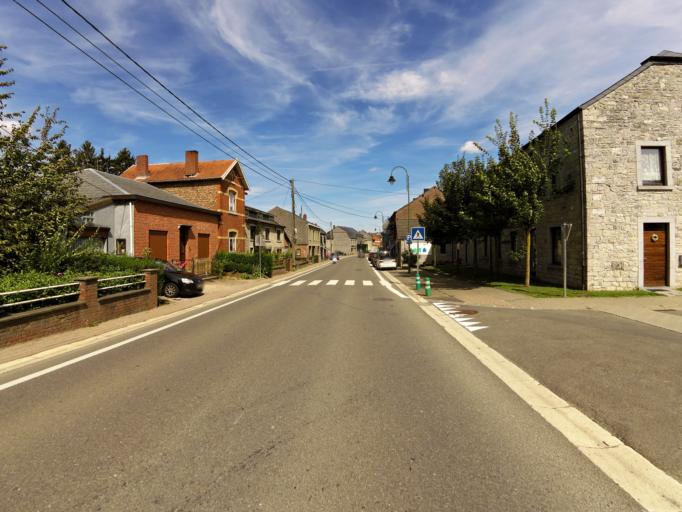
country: BE
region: Wallonia
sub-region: Province du Luxembourg
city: Hotton
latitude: 50.2663
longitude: 5.4435
